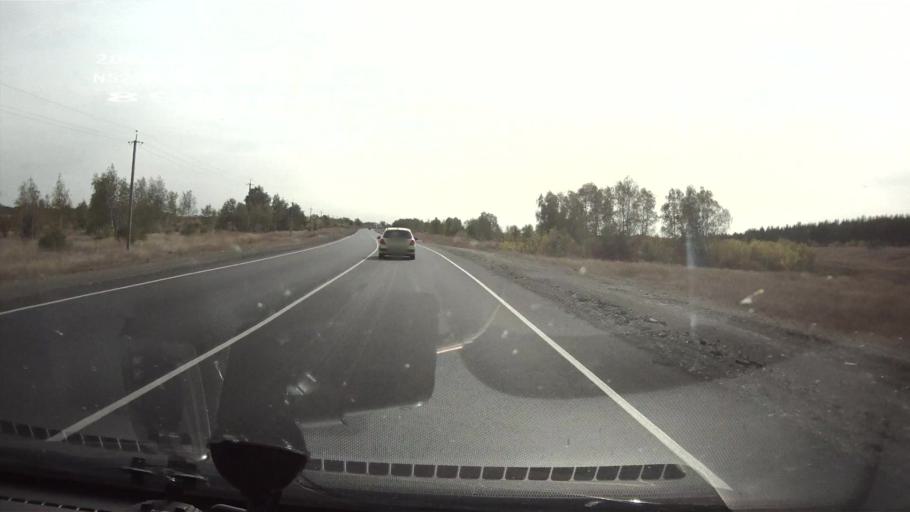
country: RU
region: Saratov
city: Sinodskoye
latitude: 52.0391
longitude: 46.7327
